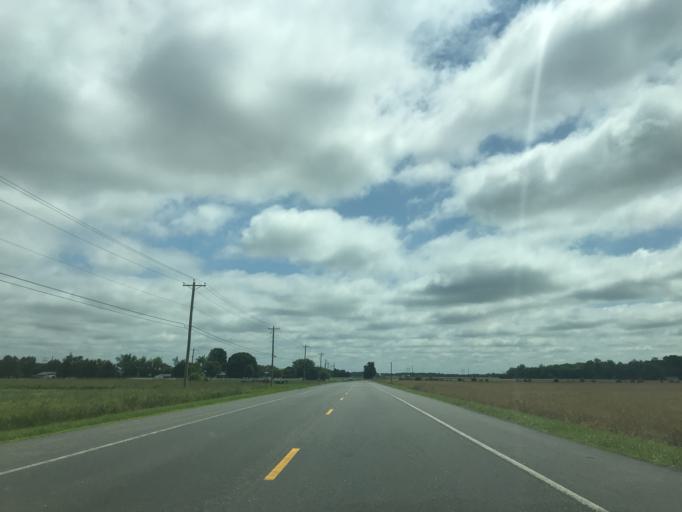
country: US
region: Maryland
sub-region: Caroline County
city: Ridgely
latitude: 38.9278
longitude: -75.9187
